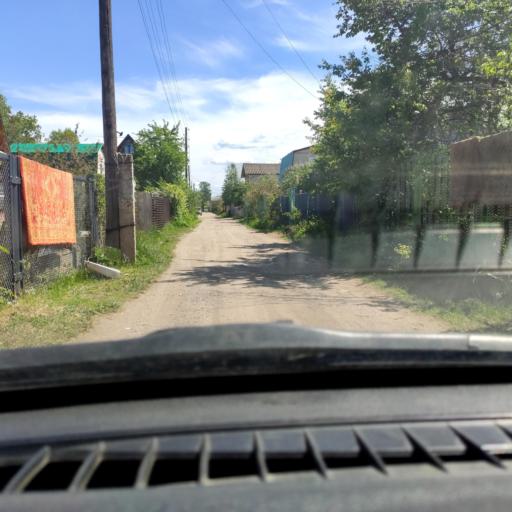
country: RU
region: Samara
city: Zhigulevsk
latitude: 53.4588
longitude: 49.5222
